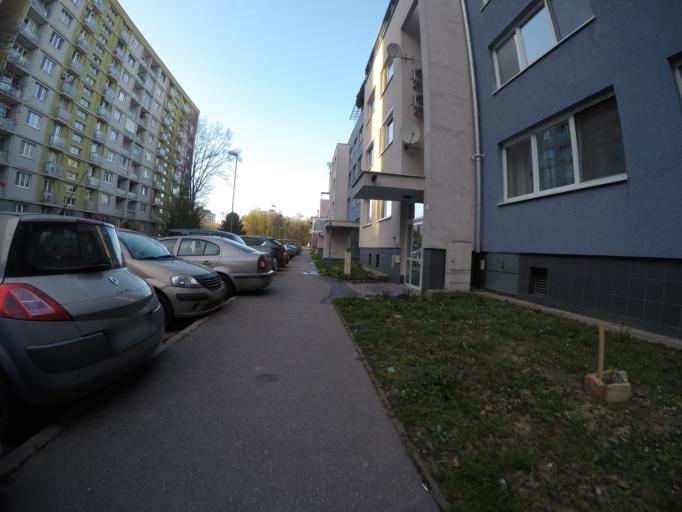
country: SK
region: Bratislavsky
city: Bratislava
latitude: 48.1554
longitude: 17.1619
